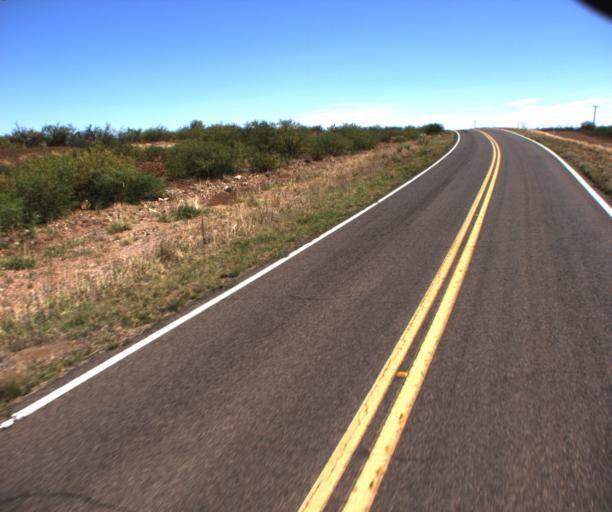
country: US
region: Arizona
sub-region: Cochise County
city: Douglas
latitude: 31.5000
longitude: -109.3233
